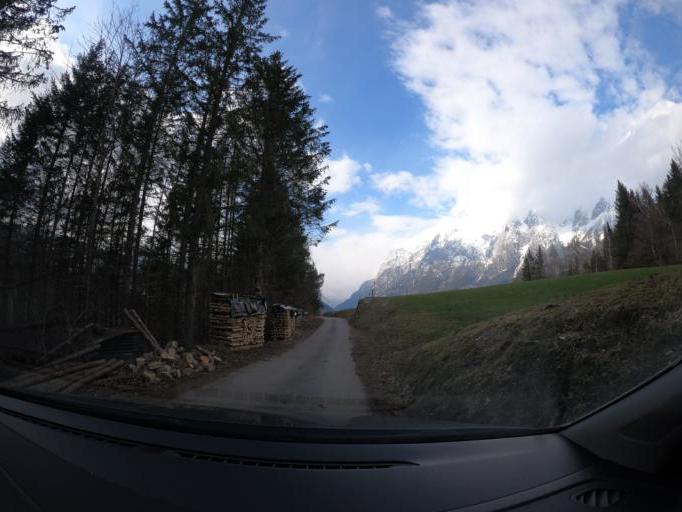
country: AT
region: Salzburg
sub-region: Politischer Bezirk Sankt Johann im Pongau
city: Pfarrwerfen
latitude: 47.4526
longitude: 13.1928
